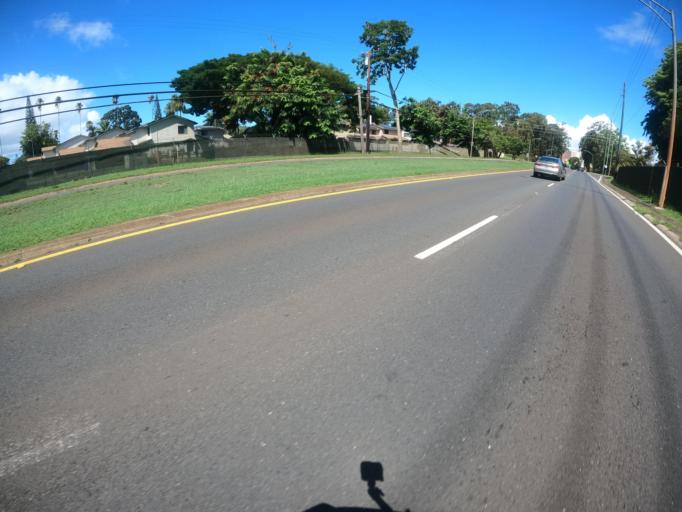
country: US
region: Hawaii
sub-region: Honolulu County
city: Wahiawa
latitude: 21.4862
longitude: -158.0419
